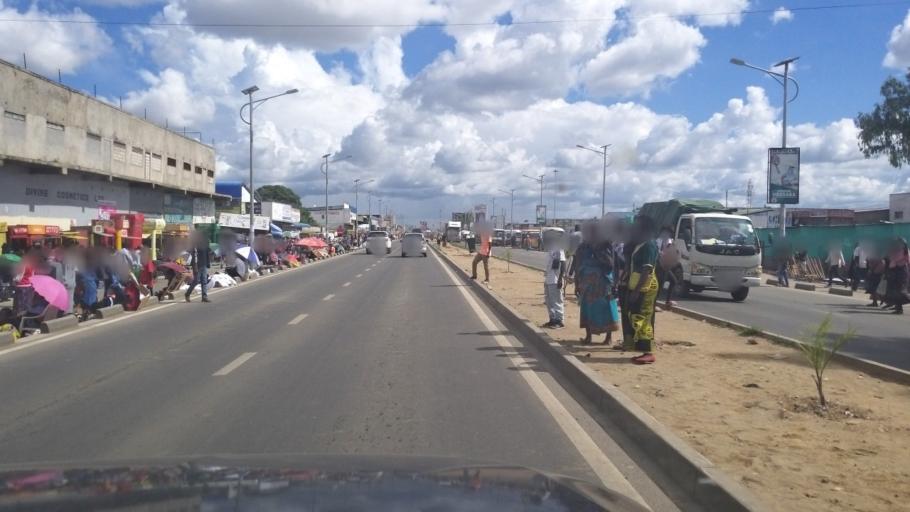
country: ZM
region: Lusaka
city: Lusaka
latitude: -15.4174
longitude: 28.2777
